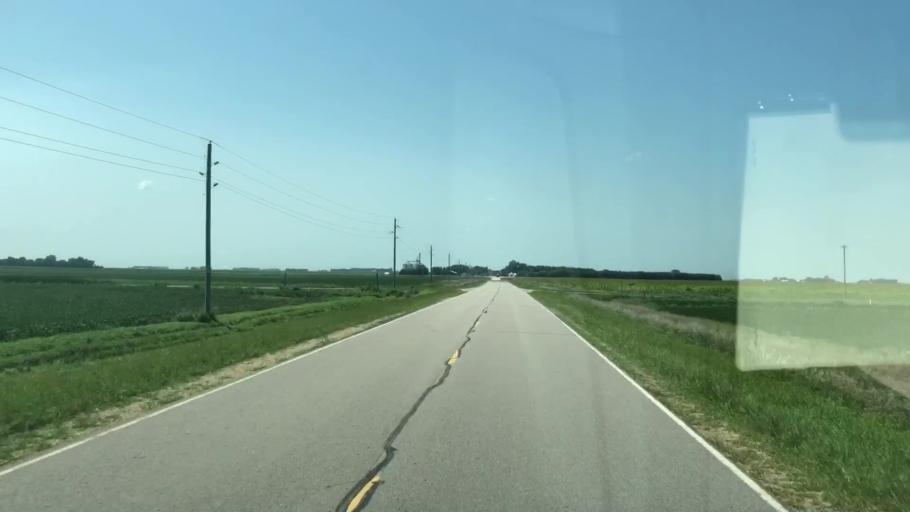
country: US
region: Iowa
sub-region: O'Brien County
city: Sheldon
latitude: 43.2443
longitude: -95.8019
